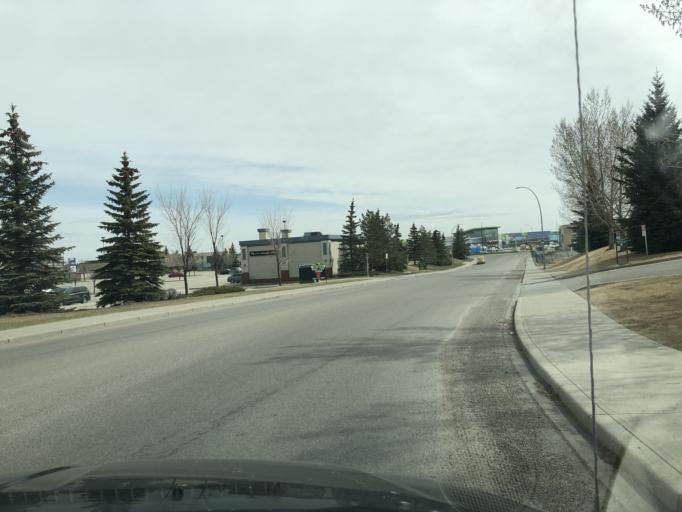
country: CA
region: Alberta
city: Calgary
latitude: 51.0728
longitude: -113.9916
